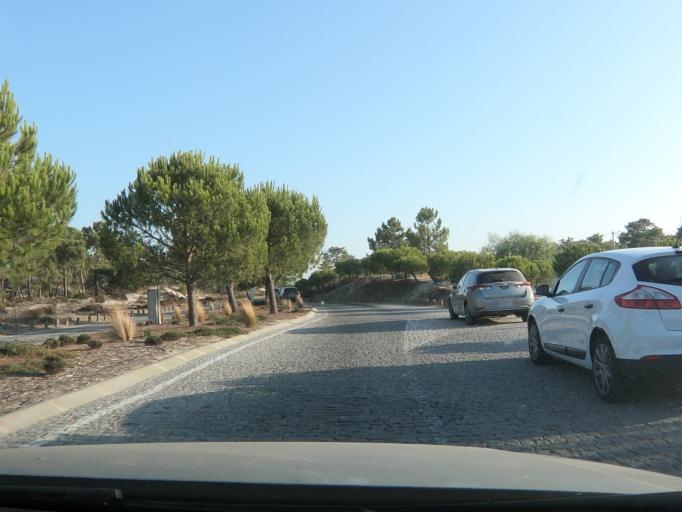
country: PT
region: Setubal
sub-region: Setubal
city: Setubal
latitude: 38.4736
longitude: -8.8852
